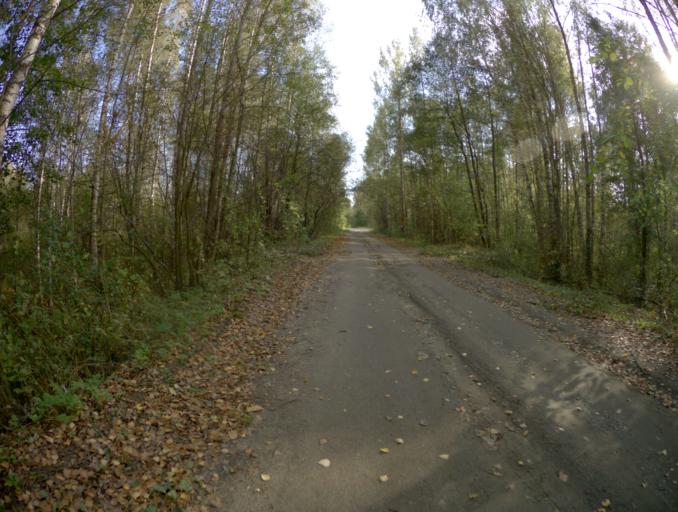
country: RU
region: Vladimir
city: Raduzhnyy
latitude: 56.0024
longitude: 40.2673
